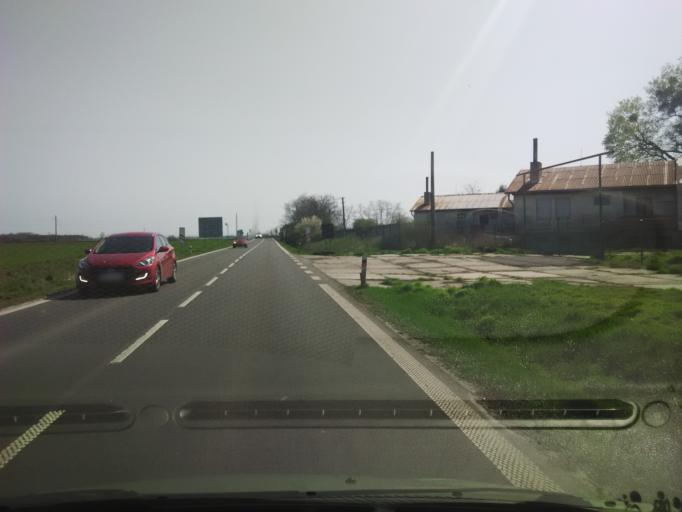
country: SK
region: Nitriansky
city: Surany
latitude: 48.0615
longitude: 18.1001
